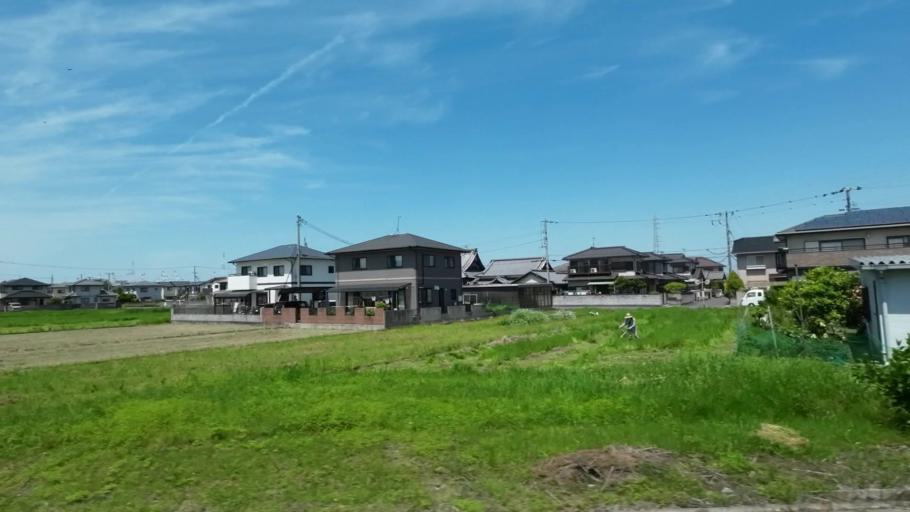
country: JP
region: Kagawa
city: Tadotsu
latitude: 34.2790
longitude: 133.7617
